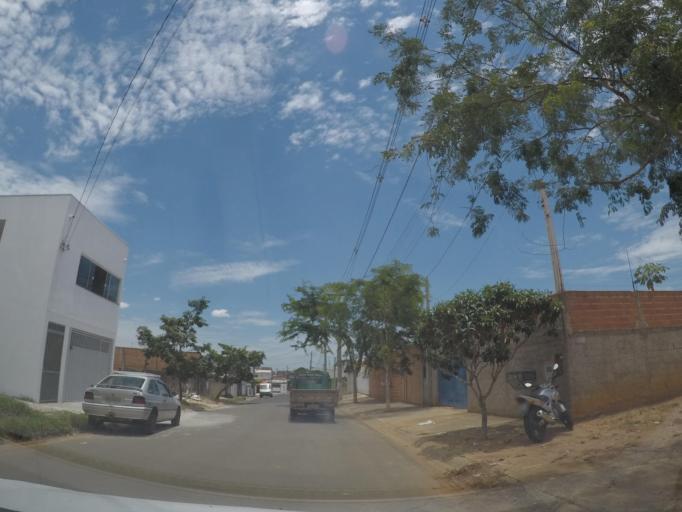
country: BR
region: Sao Paulo
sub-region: Hortolandia
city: Hortolandia
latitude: -22.8393
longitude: -47.1973
